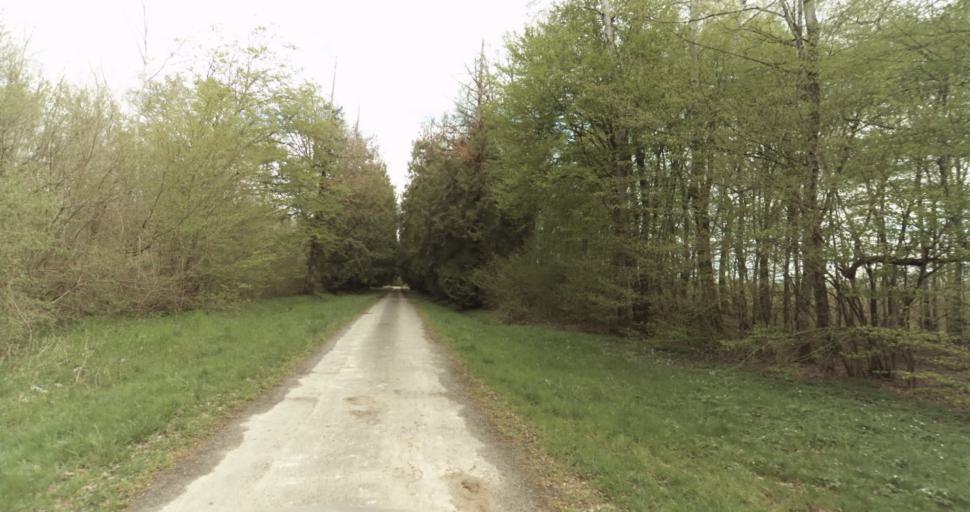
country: FR
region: Bourgogne
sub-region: Departement de la Cote-d'Or
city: Auxonne
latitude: 47.1701
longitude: 5.4263
